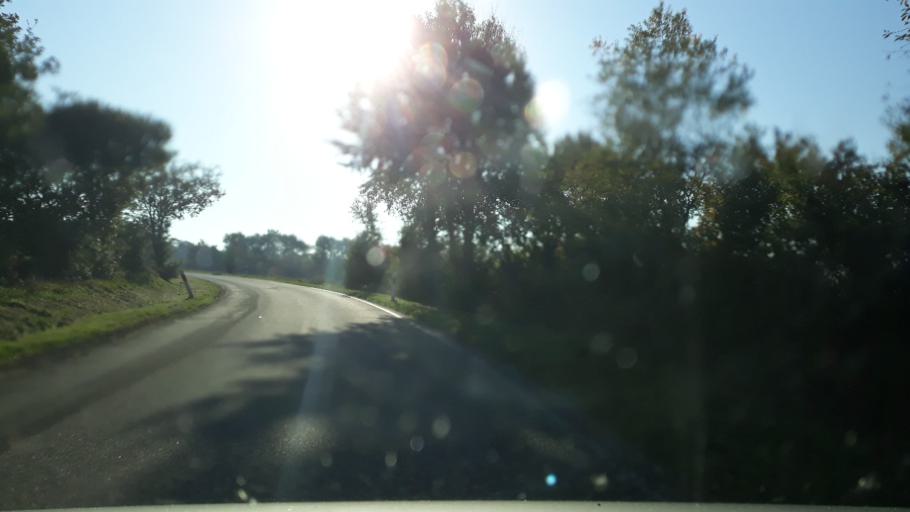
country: DE
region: Schleswig-Holstein
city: Borm
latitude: 54.3962
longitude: 9.4011
